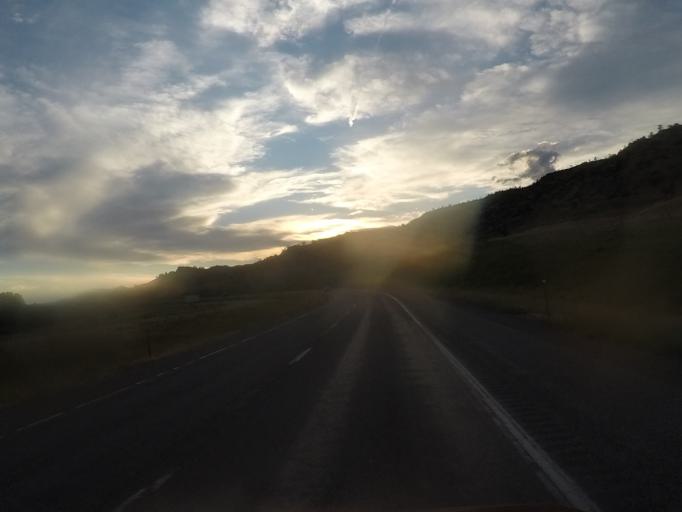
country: US
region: Montana
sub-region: Park County
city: Livingston
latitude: 45.6607
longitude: -110.6376
